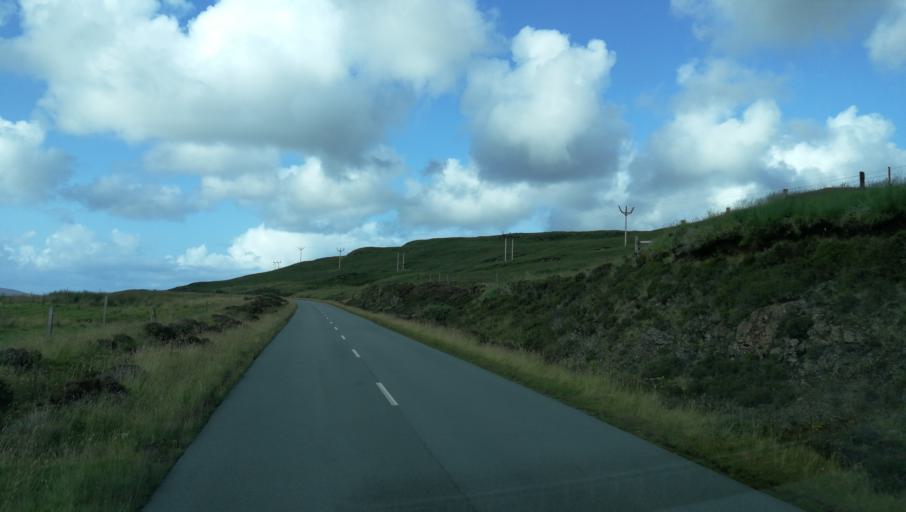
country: GB
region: Scotland
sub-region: Highland
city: Isle of Skye
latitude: 57.4580
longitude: -6.5417
